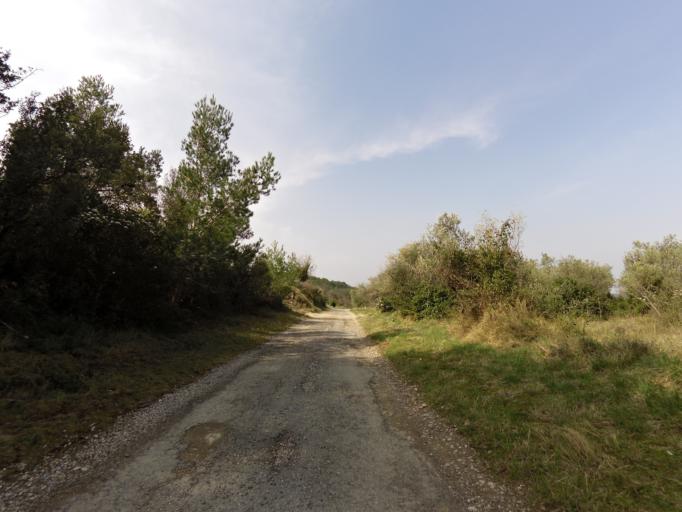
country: FR
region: Languedoc-Roussillon
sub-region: Departement du Gard
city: Congenies
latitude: 43.7661
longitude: 4.1620
